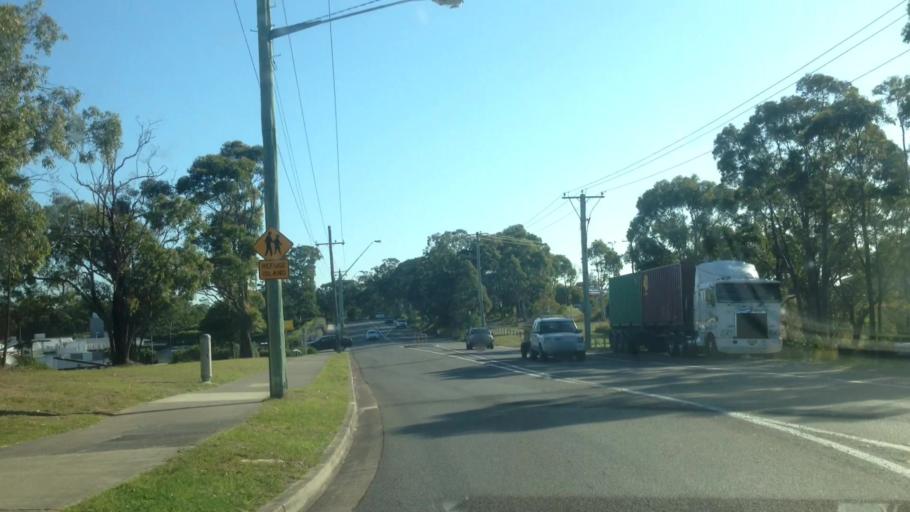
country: AU
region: New South Wales
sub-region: Lake Macquarie Shire
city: Dora Creek
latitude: -33.1092
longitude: 151.5340
